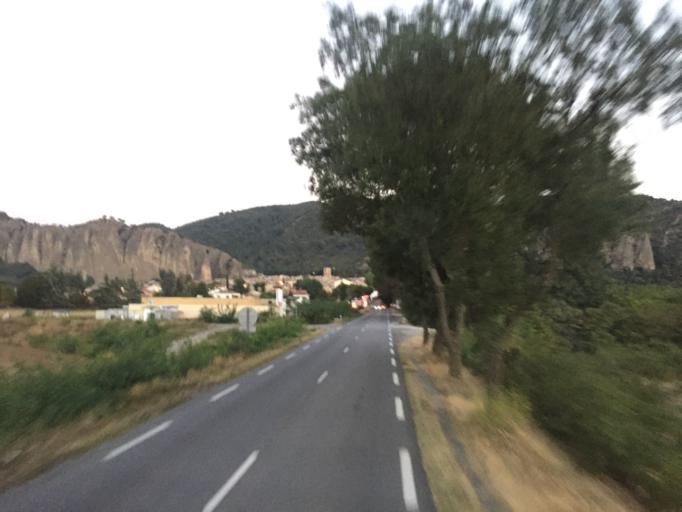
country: FR
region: Provence-Alpes-Cote d'Azur
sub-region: Departement des Alpes-de-Haute-Provence
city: Les Mees
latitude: 44.0329
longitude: 5.9689
